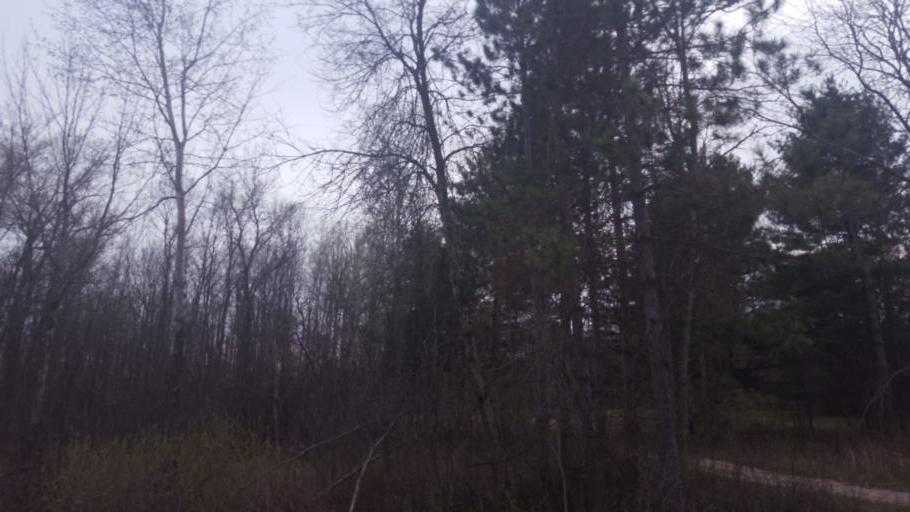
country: US
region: Michigan
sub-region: Clare County
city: Clare
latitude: 43.8731
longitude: -84.6494
